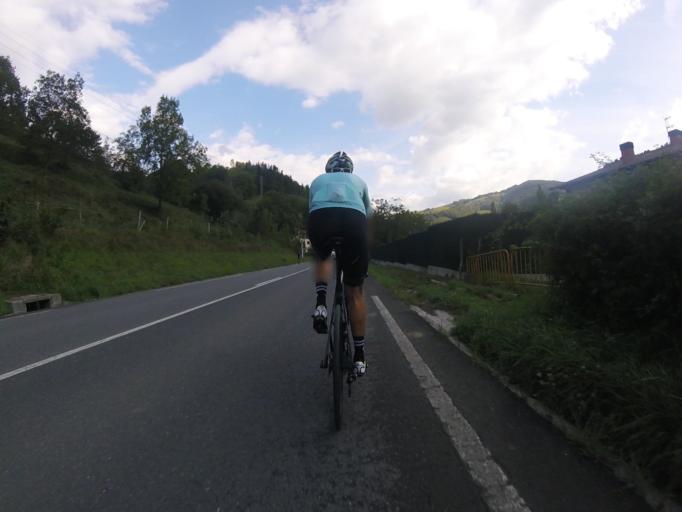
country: ES
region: Basque Country
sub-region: Provincia de Guipuzcoa
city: Amezqueta
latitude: 43.0623
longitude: -2.0874
